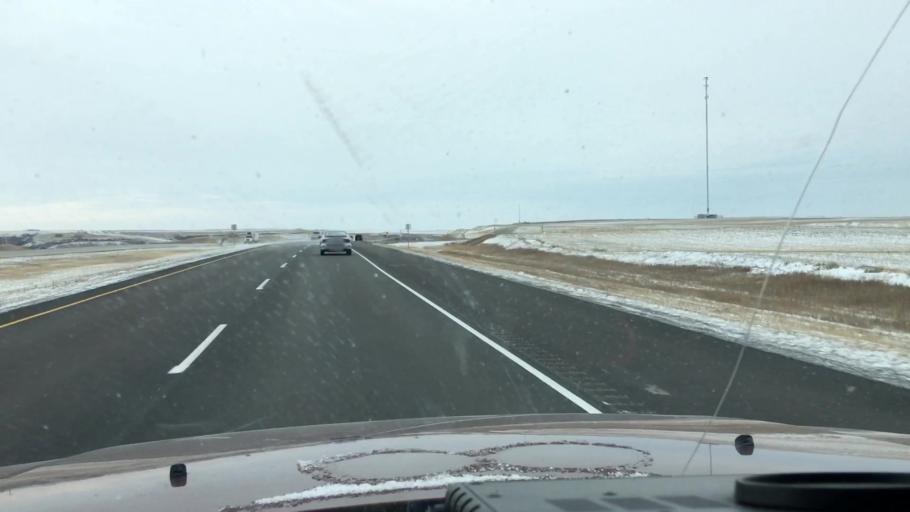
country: CA
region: Saskatchewan
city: Saskatoon
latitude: 51.7413
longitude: -106.4763
